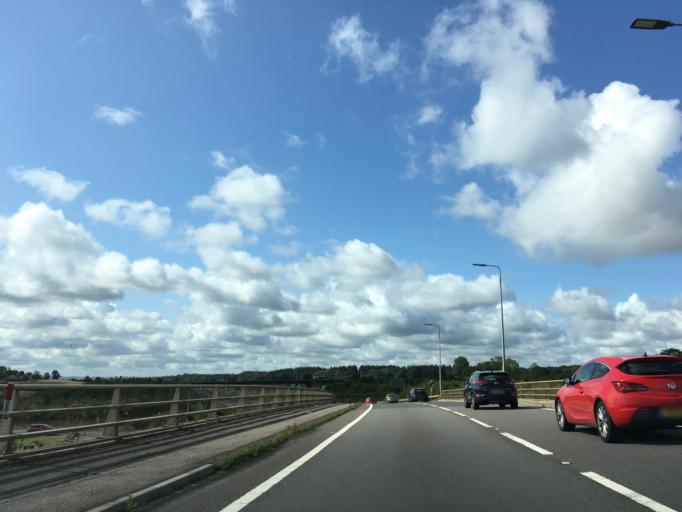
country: GB
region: England
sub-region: West Berkshire
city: Winterbourne
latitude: 51.4495
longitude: -1.3123
